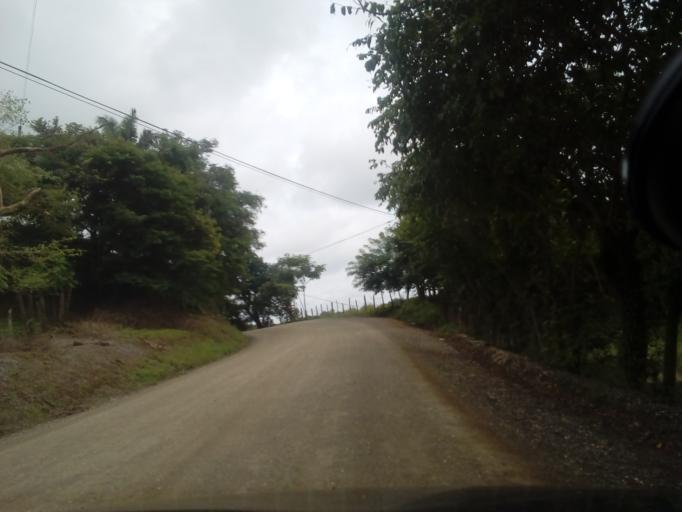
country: CR
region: Guanacaste
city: Samara
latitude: 9.9198
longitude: -85.5625
